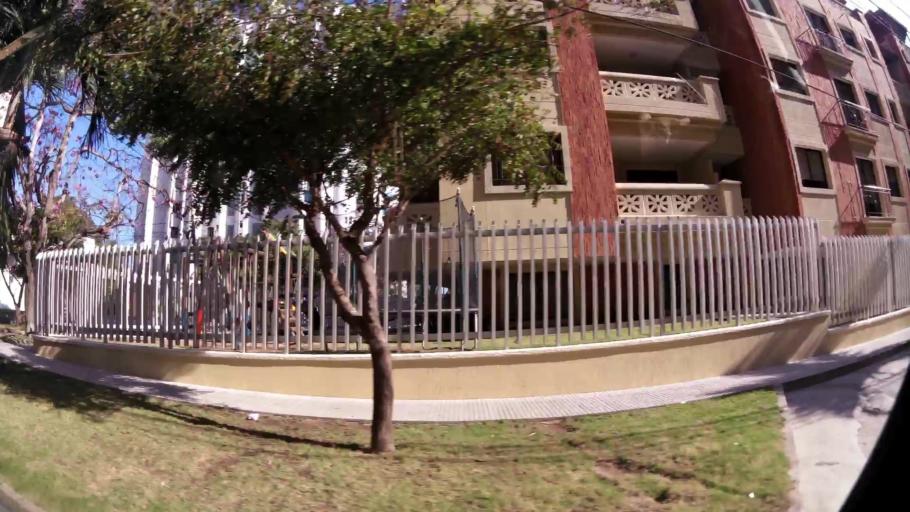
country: CO
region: Atlantico
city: Barranquilla
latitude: 11.0089
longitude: -74.8093
